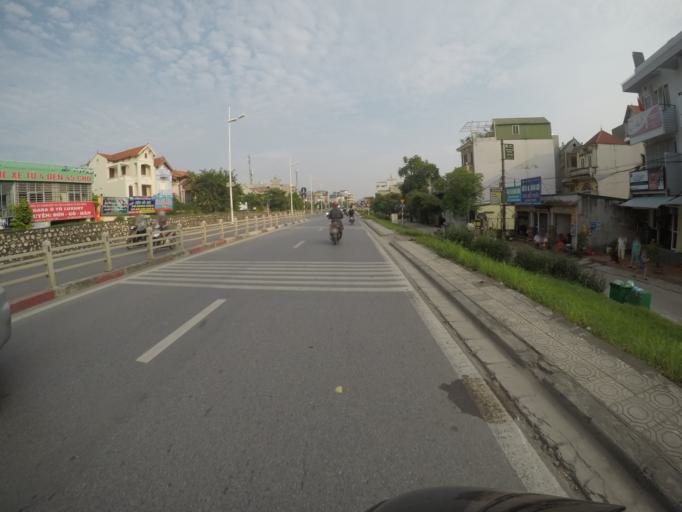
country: VN
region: Ha Noi
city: Tay Ho
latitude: 21.0744
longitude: 105.8238
